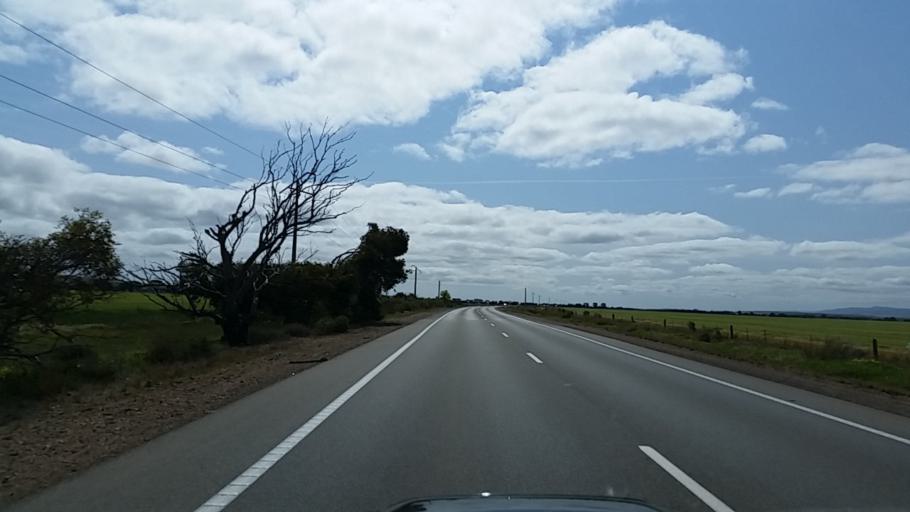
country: AU
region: South Australia
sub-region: Port Pirie City and Dists
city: Crystal Brook
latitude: -33.4744
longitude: 138.1673
